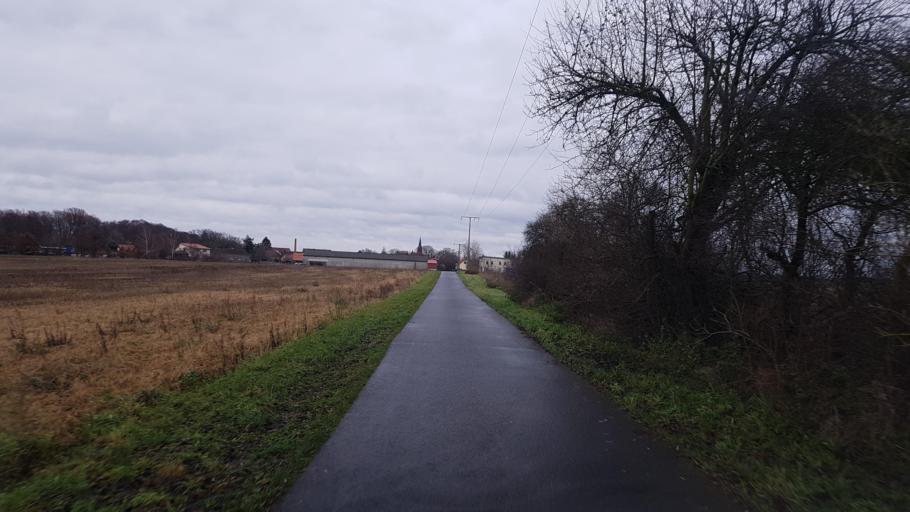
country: DE
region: Brandenburg
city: Tauche
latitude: 52.0850
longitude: 14.1568
